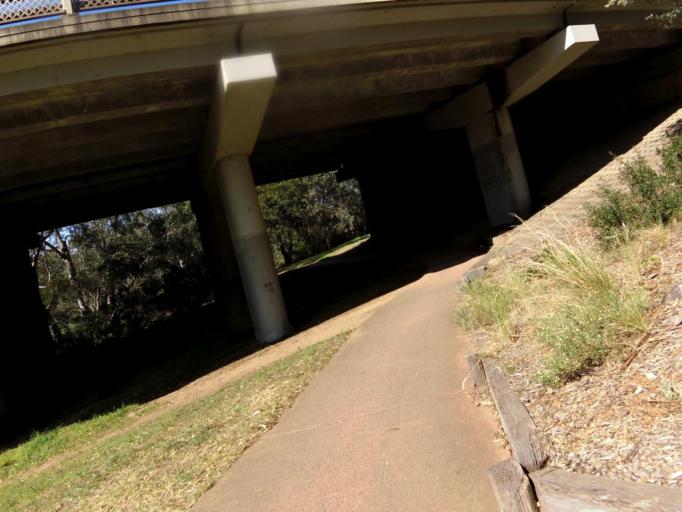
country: AU
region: Victoria
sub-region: Wyndham
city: Werribee
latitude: -37.9038
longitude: 144.6543
